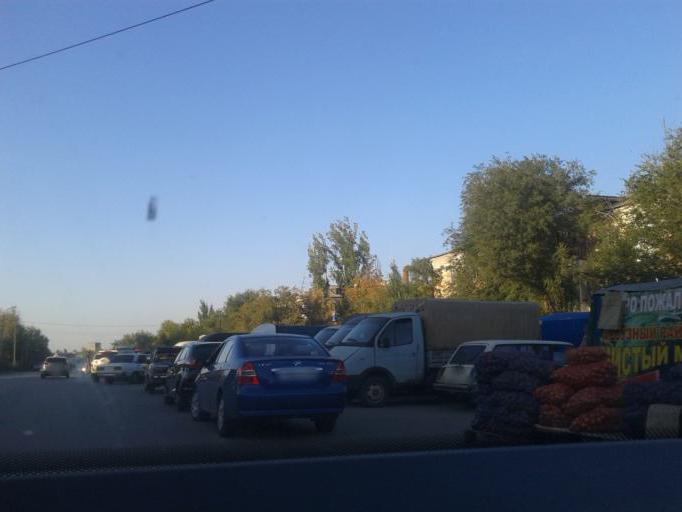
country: RU
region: Volgograd
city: Gorodishche
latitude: 48.7693
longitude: 44.4779
